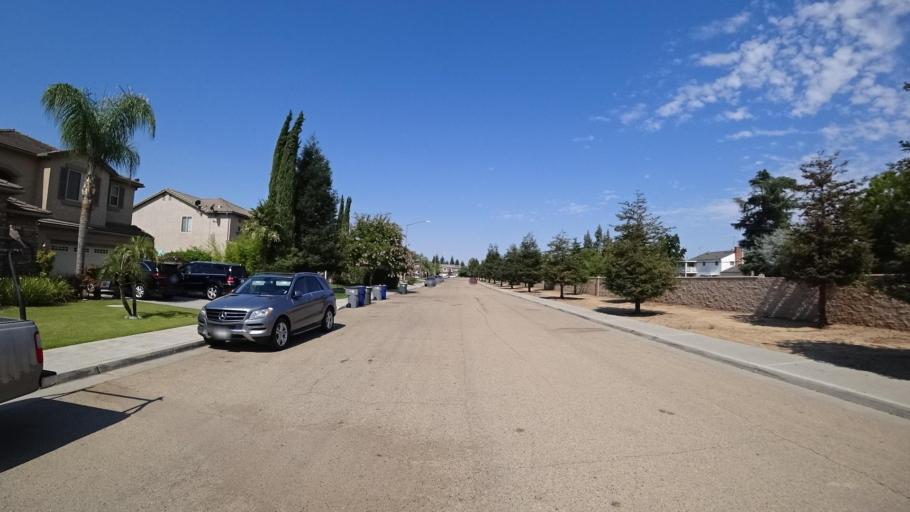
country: US
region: California
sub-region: Fresno County
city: Sunnyside
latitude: 36.7219
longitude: -119.6831
